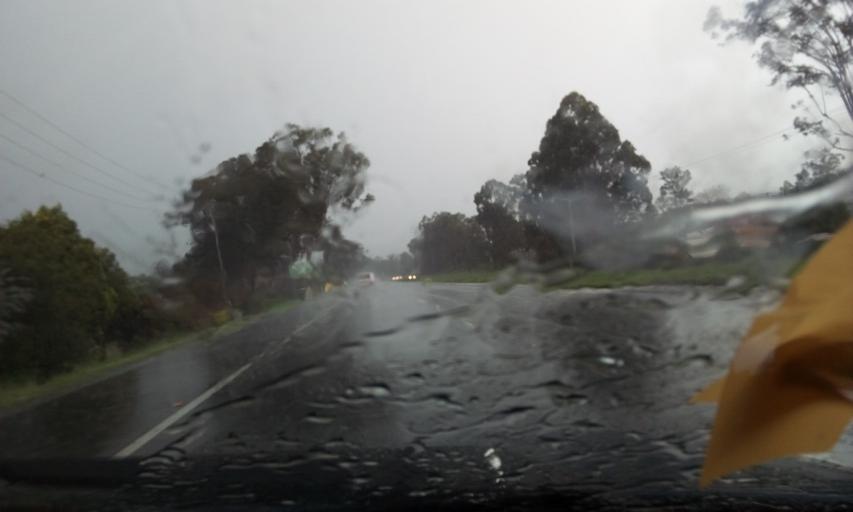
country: AU
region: New South Wales
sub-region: Camden
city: Camden South
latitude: -34.0788
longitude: 150.6949
